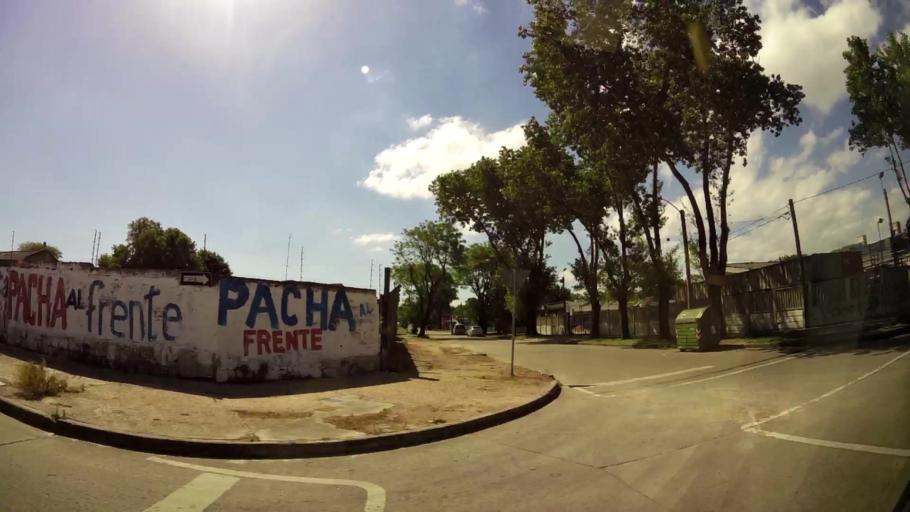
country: UY
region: Montevideo
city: Montevideo
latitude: -34.8658
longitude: -56.2260
